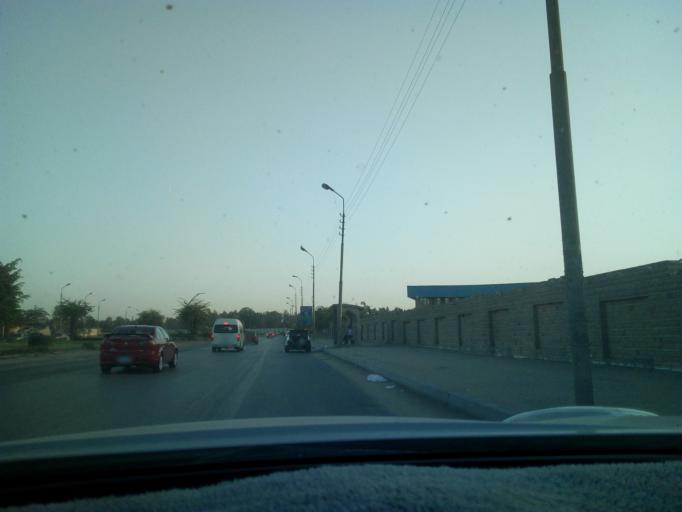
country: EG
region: Muhafazat al Qalyubiyah
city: Al Khankah
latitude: 30.1196
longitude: 31.3637
